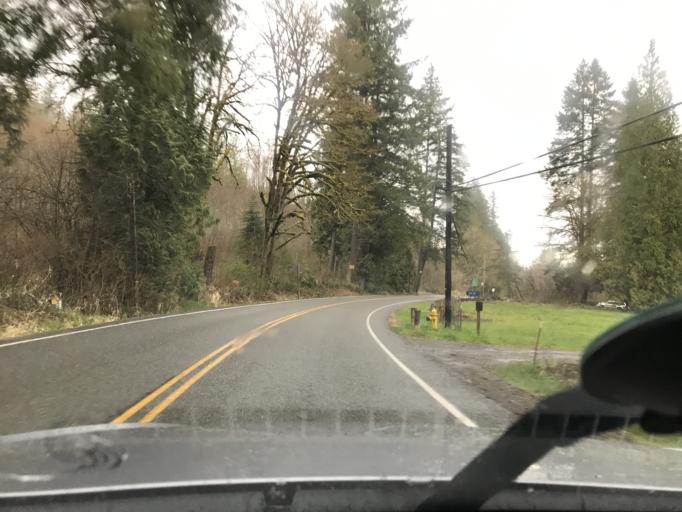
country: US
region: Washington
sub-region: King County
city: Ames Lake
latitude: 47.6516
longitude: -121.9624
